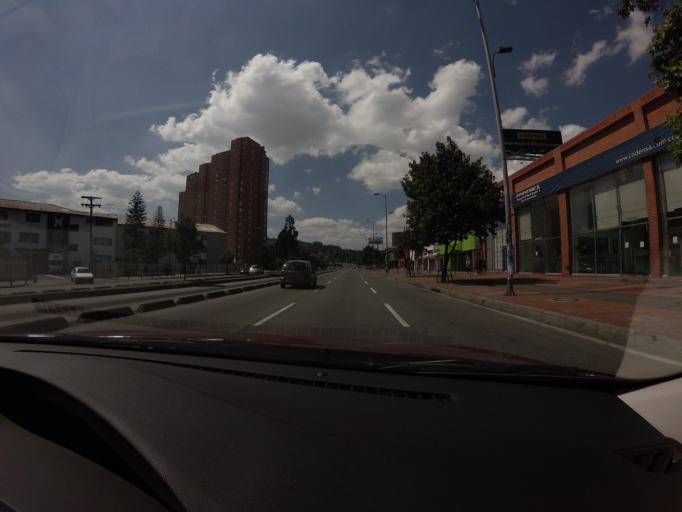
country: CO
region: Bogota D.C.
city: Barrio San Luis
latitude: 4.7164
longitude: -74.0733
